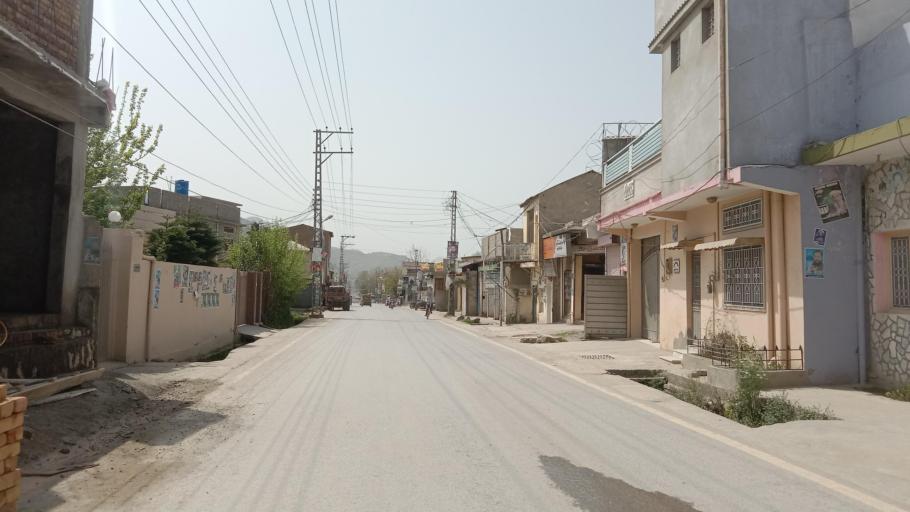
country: PK
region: Khyber Pakhtunkhwa
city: Abbottabad
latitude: 34.1646
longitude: 73.2601
